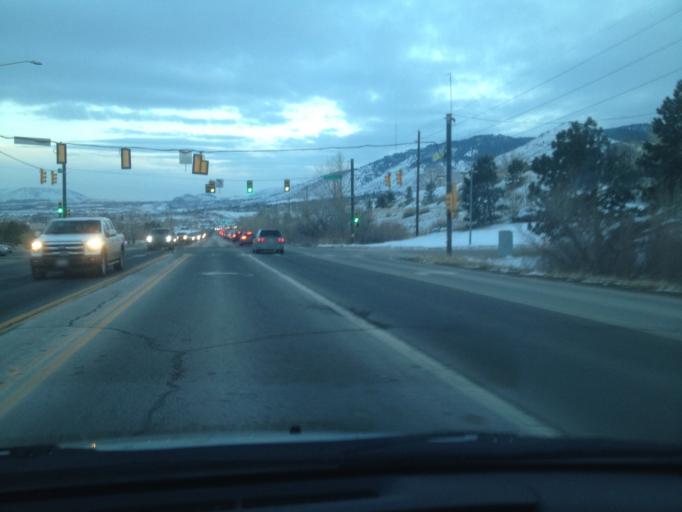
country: US
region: Colorado
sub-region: Jefferson County
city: Golden
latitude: 39.7682
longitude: -105.2356
